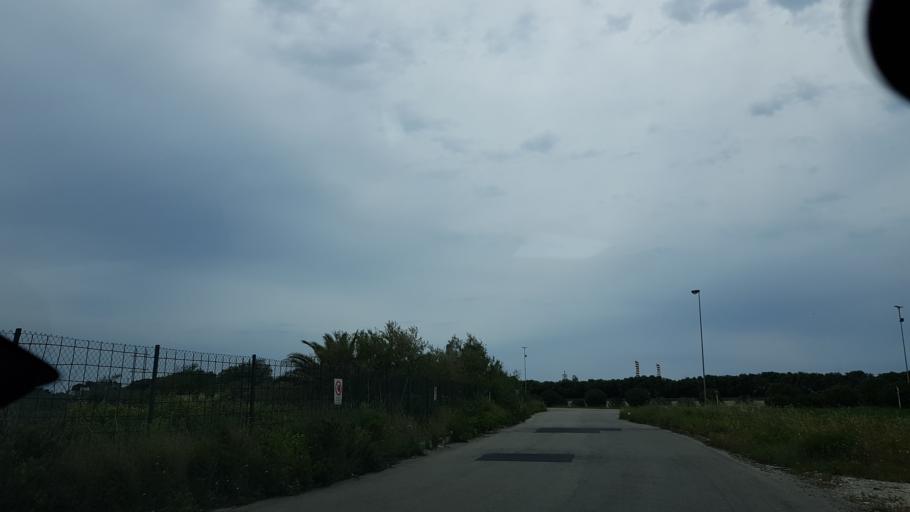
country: IT
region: Apulia
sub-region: Provincia di Brindisi
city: Materdomini
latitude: 40.6430
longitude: 17.9841
